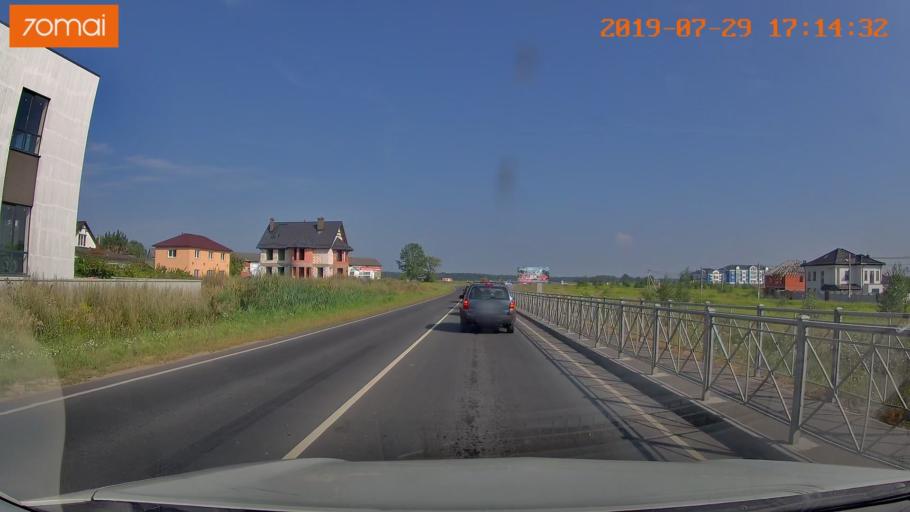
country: RU
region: Kaliningrad
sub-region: Gorod Kaliningrad
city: Kaliningrad
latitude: 54.7848
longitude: 20.4082
